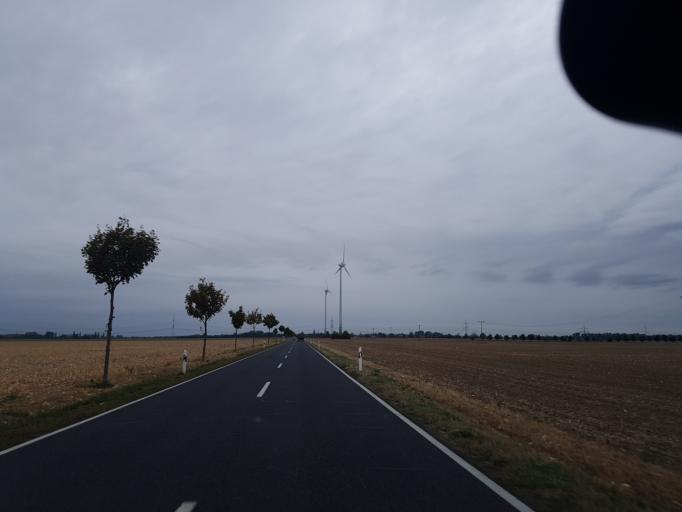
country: DE
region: Saxony-Anhalt
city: Prettin
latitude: 51.6831
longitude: 12.9032
